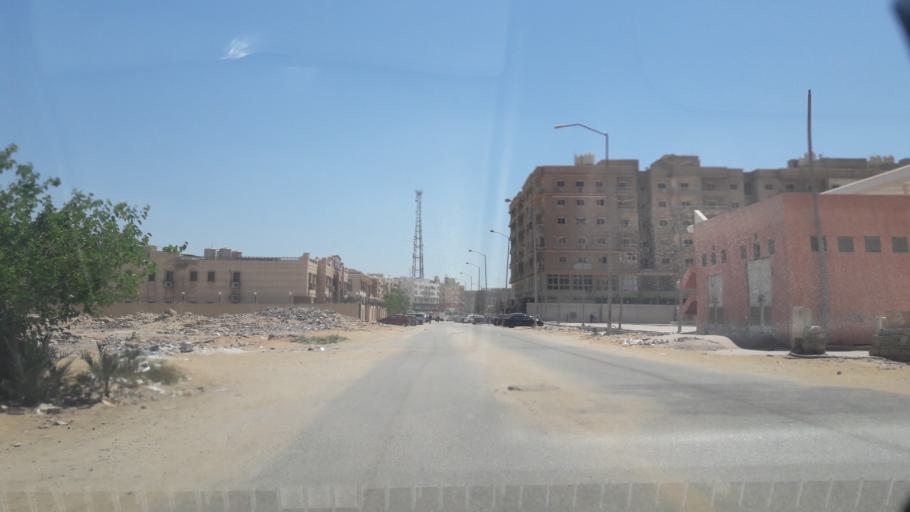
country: EG
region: Al Jizah
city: Madinat Sittah Uktubar
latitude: 29.9668
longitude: 30.9324
